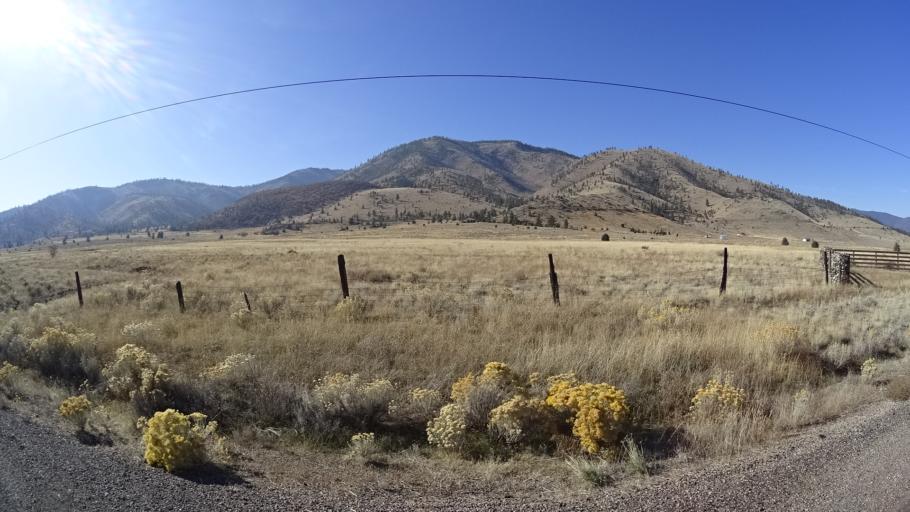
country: US
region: California
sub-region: Siskiyou County
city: Weed
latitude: 41.4807
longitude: -122.4924
